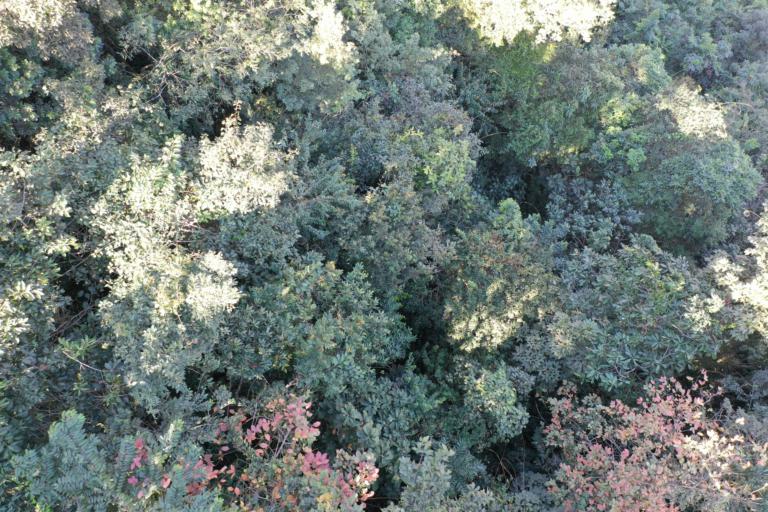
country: BO
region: La Paz
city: Mapiri
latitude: -15.3053
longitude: -68.2152
